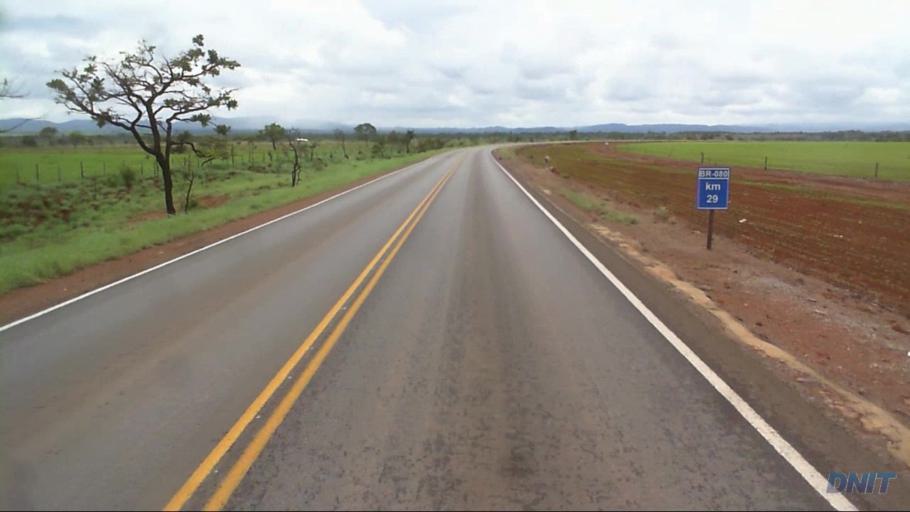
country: BR
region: Goias
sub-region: Padre Bernardo
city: Padre Bernardo
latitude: -15.3028
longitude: -48.2301
